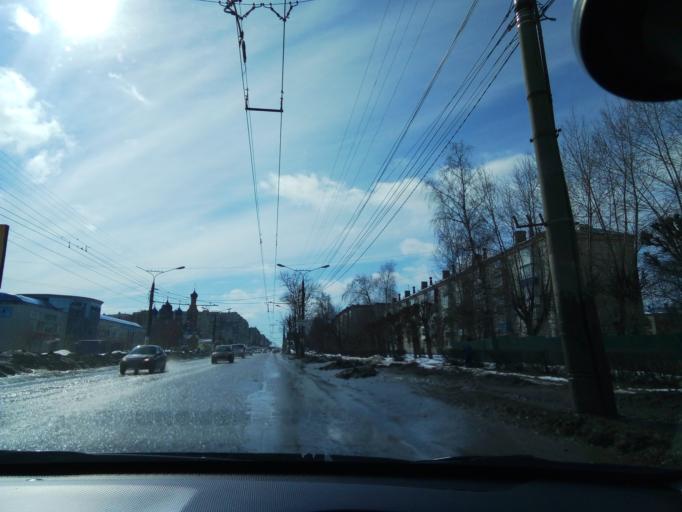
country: RU
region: Chuvashia
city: Novyye Lapsary
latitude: 56.1208
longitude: 47.1984
